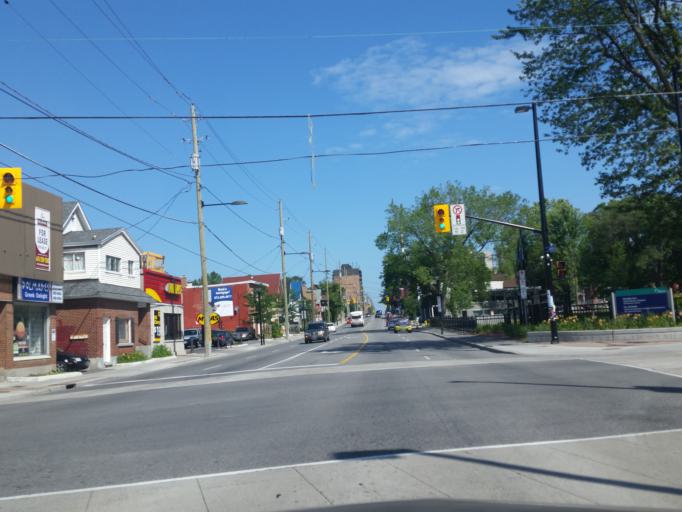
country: CA
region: Ontario
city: Ottawa
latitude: 45.4078
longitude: -75.7036
